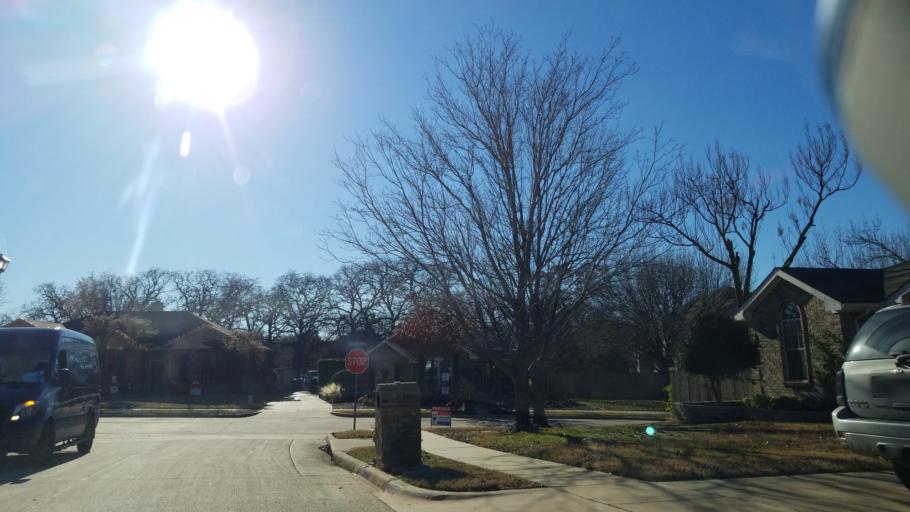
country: US
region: Texas
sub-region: Denton County
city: Corinth
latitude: 33.1373
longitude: -97.0792
